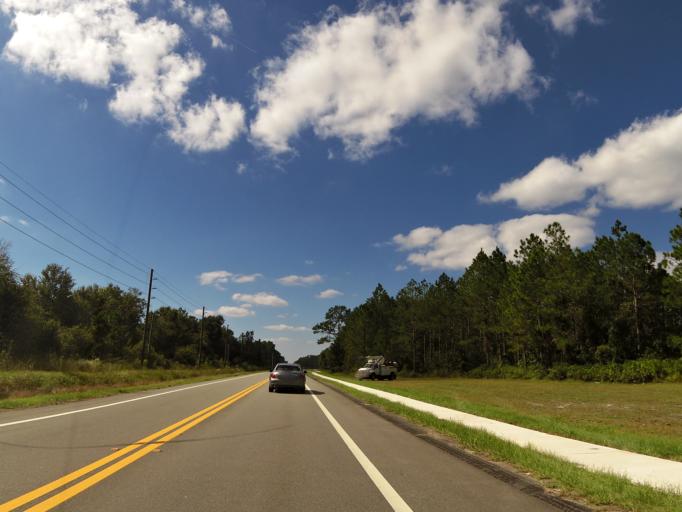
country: US
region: Florida
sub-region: Saint Johns County
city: Fruit Cove
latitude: 30.0603
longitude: -81.6398
